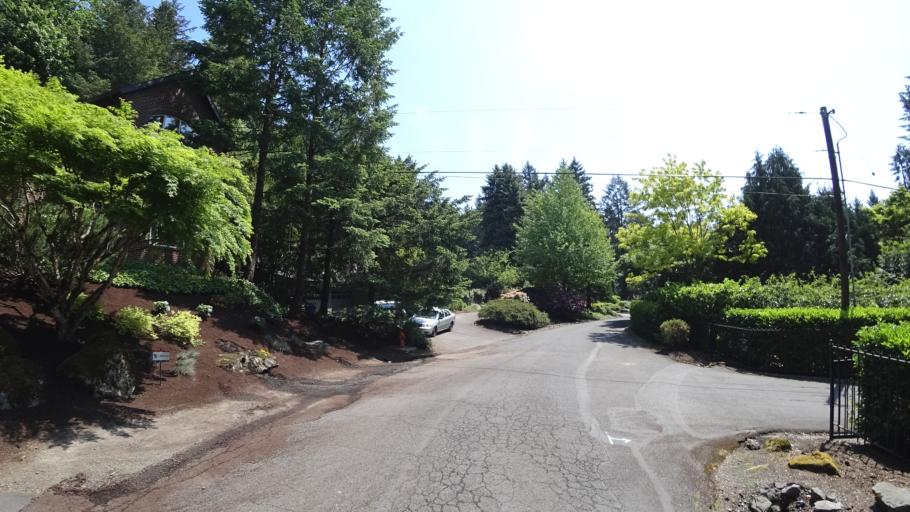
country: US
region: Oregon
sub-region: Washington County
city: West Slope
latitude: 45.5125
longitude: -122.7235
